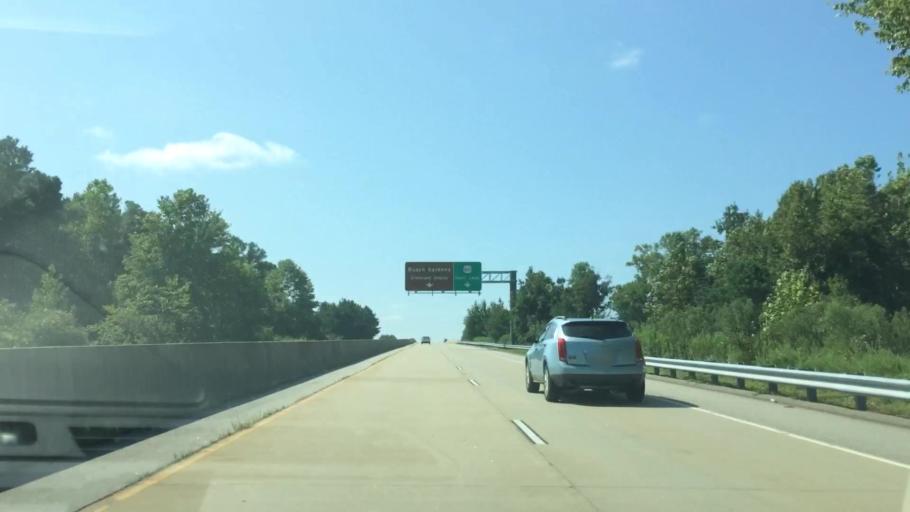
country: US
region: Virginia
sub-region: City of Williamsburg
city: Williamsburg
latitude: 37.2447
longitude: -76.6343
